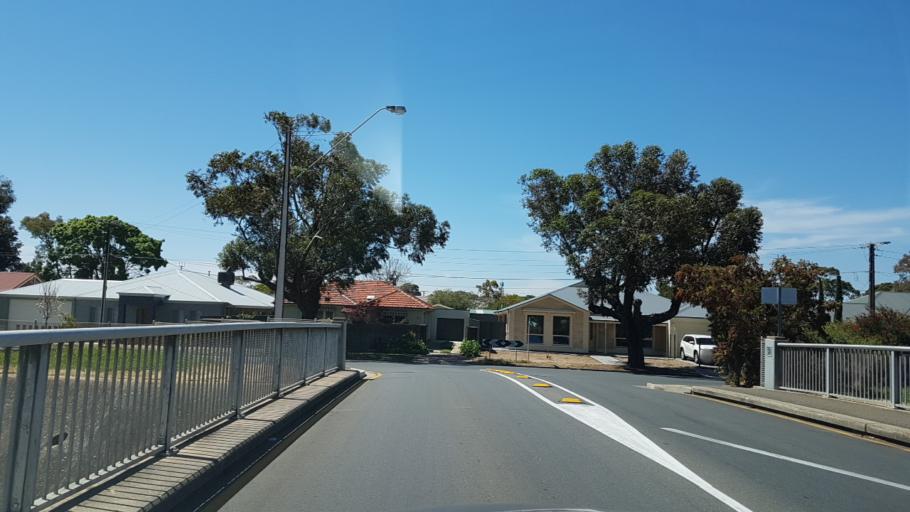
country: AU
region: South Australia
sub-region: Holdfast Bay
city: Glenelg East
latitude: -34.9682
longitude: 138.5222
